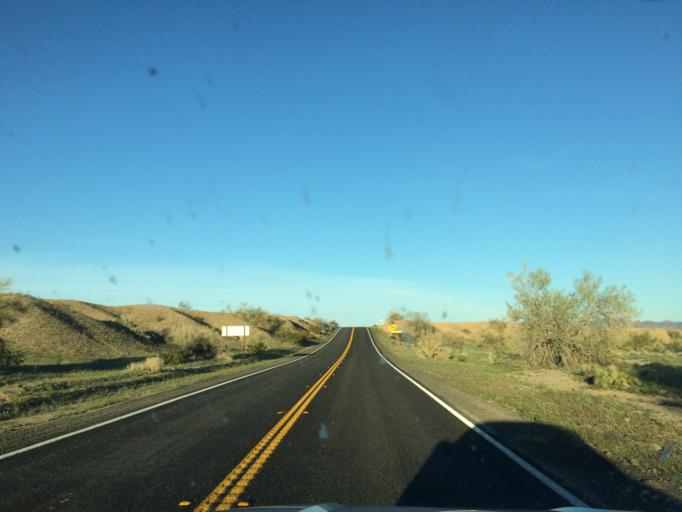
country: US
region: California
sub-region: Riverside County
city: Mesa Verde
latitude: 33.2828
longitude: -114.7784
